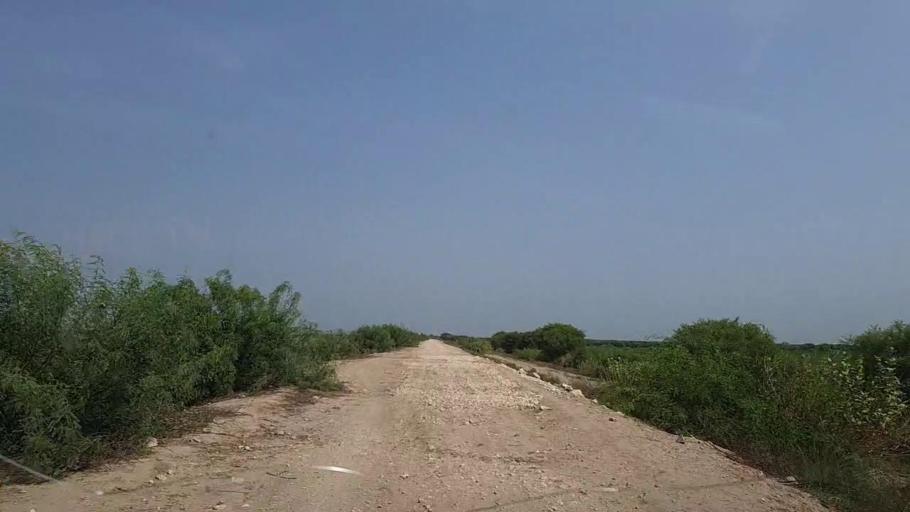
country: PK
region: Sindh
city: Ghotki
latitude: 28.1053
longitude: 69.3972
